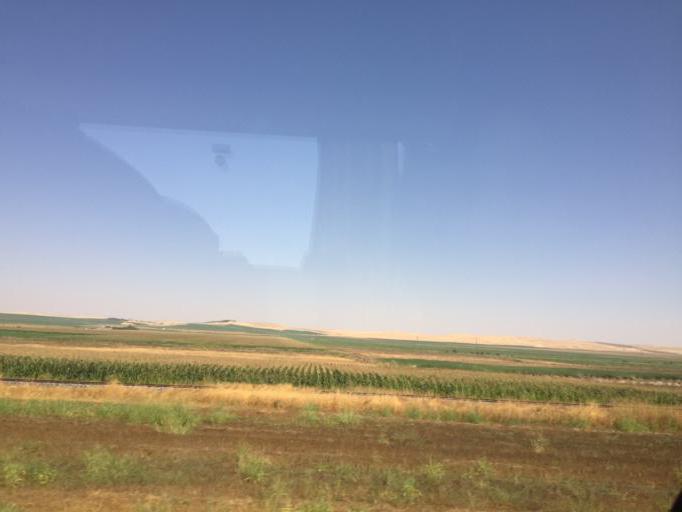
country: TR
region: Diyarbakir
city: Tepe
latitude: 37.8497
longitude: 40.7855
